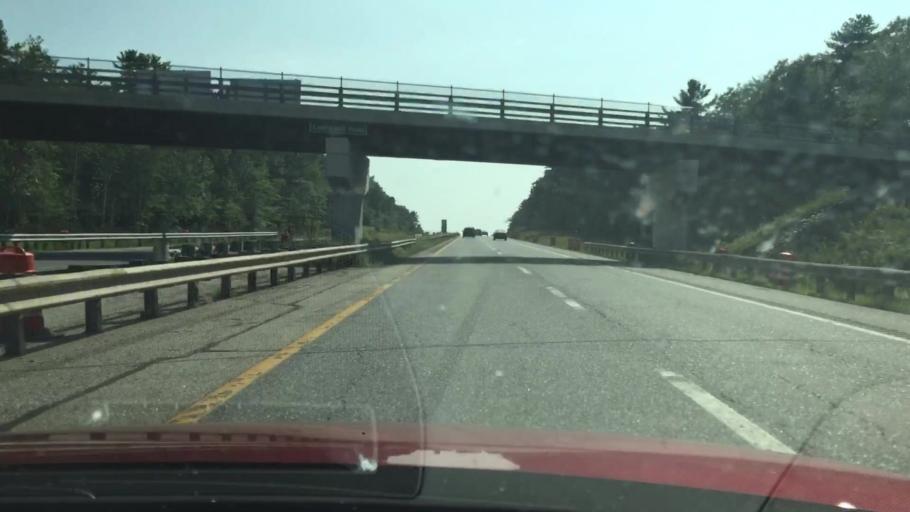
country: US
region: Maine
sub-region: Kennebec County
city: Gardiner
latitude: 44.1773
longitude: -69.8621
